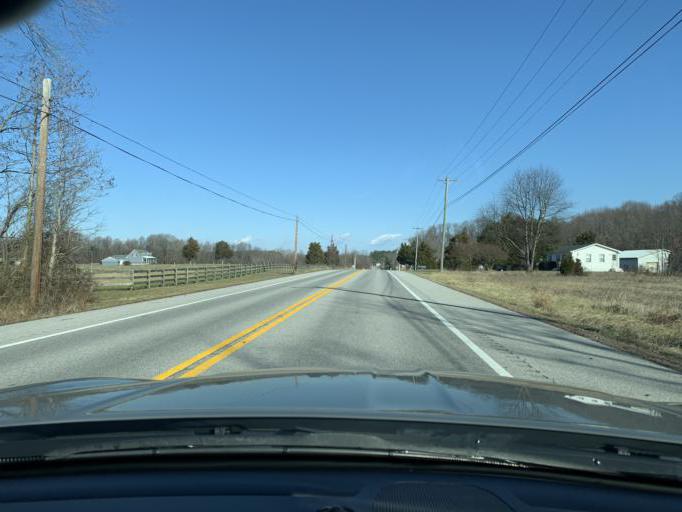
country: US
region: Maryland
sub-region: Queen Anne's County
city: Centreville
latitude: 39.1036
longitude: -76.0318
